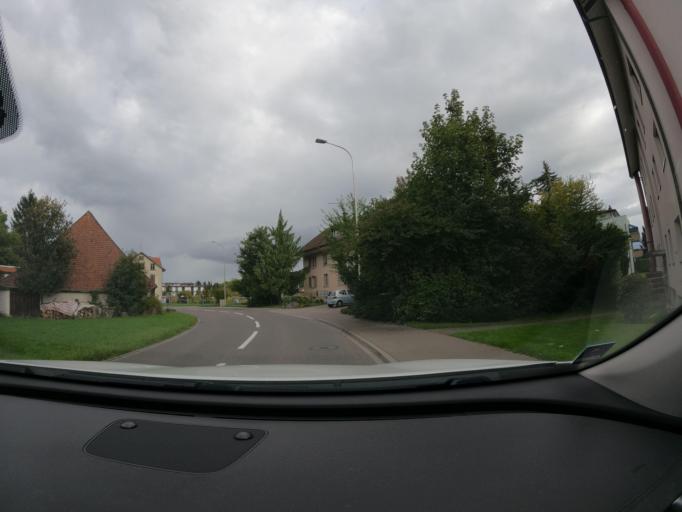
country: CH
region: Aargau
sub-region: Bezirk Kulm
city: Reinach
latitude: 47.2562
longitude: 8.1724
